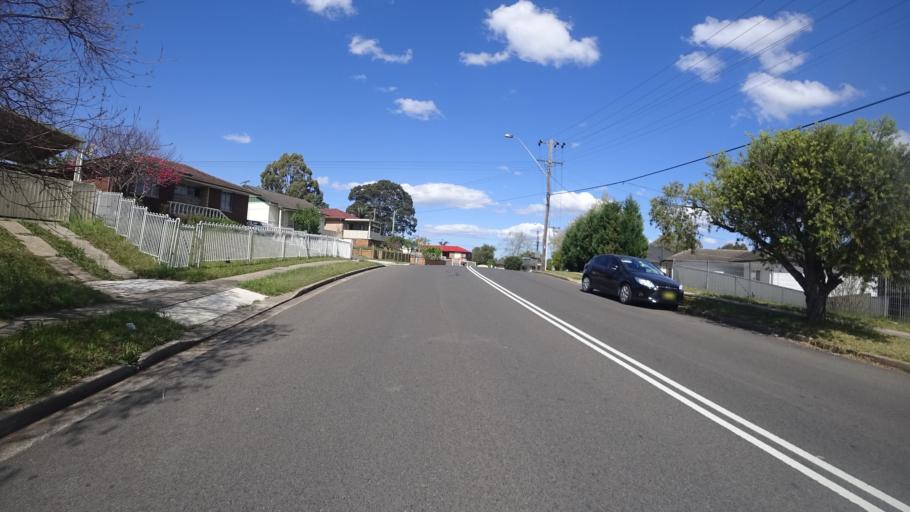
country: AU
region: New South Wales
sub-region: Fairfield
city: Cabramatta West
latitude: -33.9055
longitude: 150.9085
